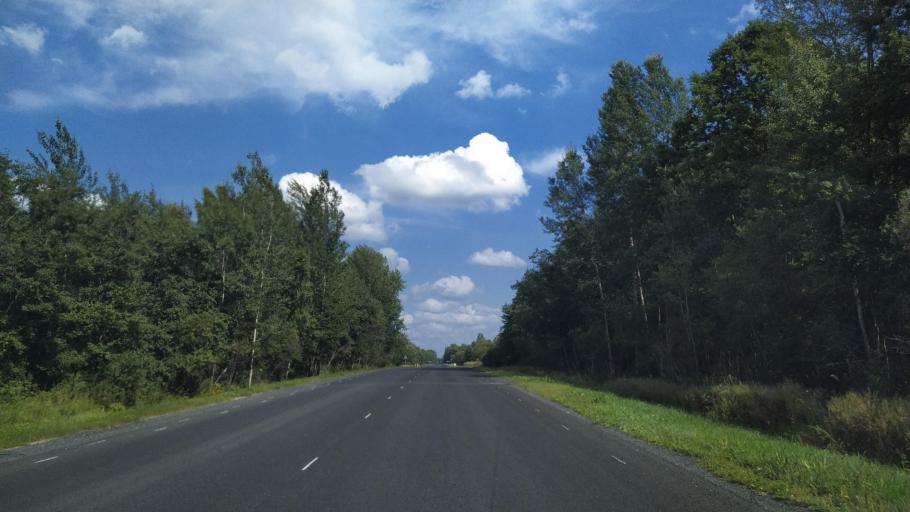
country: RU
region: Pskov
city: Porkhov
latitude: 57.7276
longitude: 29.3095
